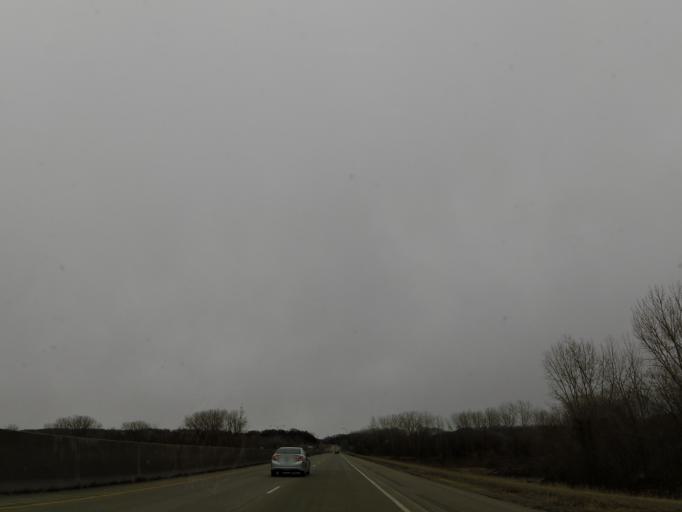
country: US
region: Minnesota
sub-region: Le Sueur County
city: Le Sueur
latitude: 44.4799
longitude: -93.9095
